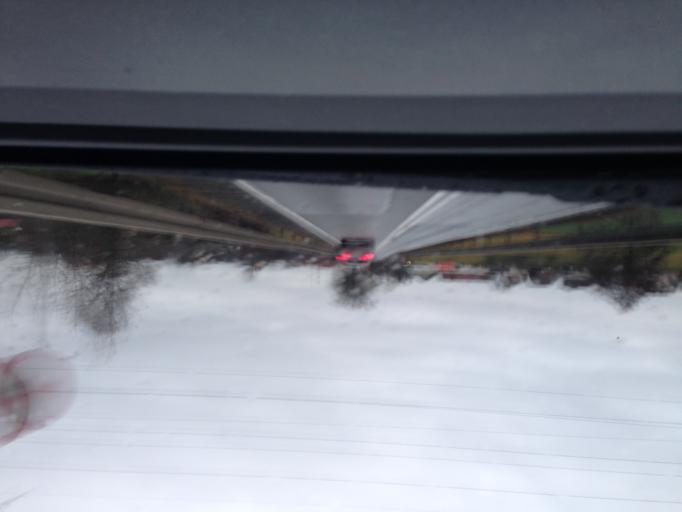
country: PL
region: Opole Voivodeship
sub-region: Powiat opolski
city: Opole
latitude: 50.6999
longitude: 17.9633
